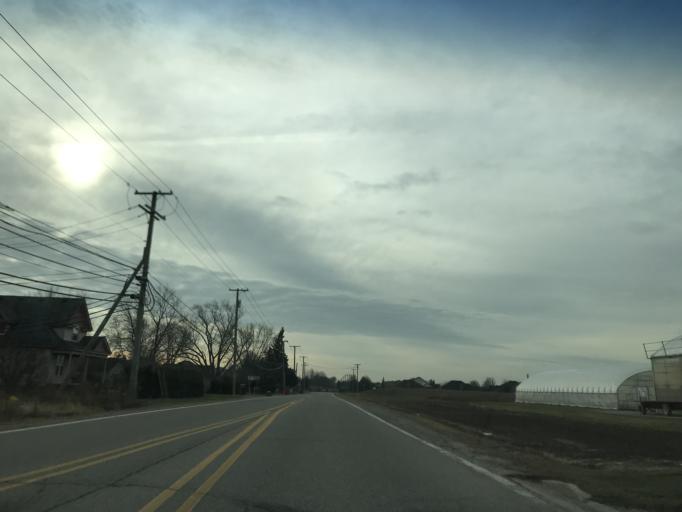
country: US
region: Michigan
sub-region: Macomb County
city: Shelby
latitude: 42.7002
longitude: -82.9589
